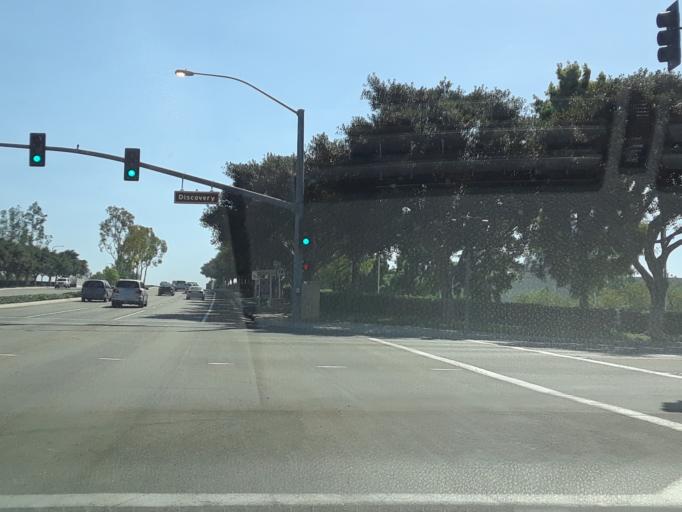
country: US
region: California
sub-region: Orange County
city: Laguna Woods
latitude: 33.6644
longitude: -117.7575
